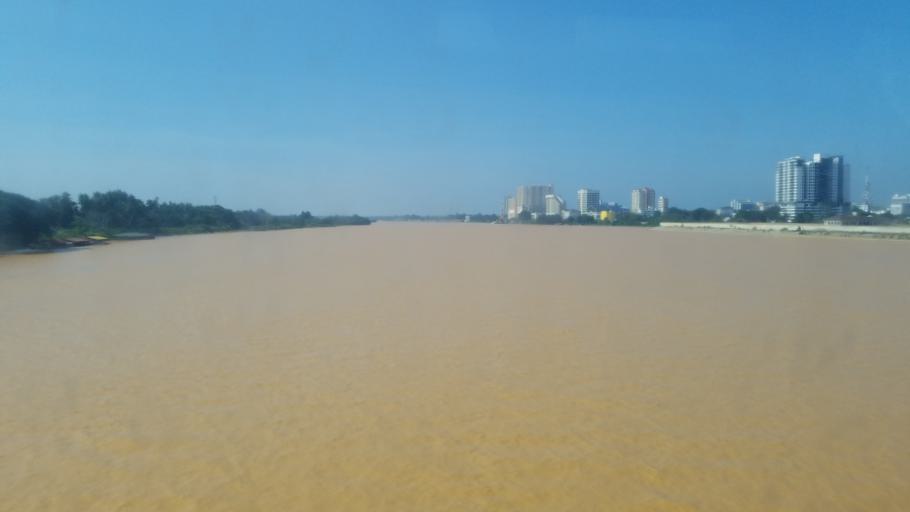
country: MY
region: Kelantan
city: Kota Bharu
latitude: 6.1165
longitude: 102.2284
